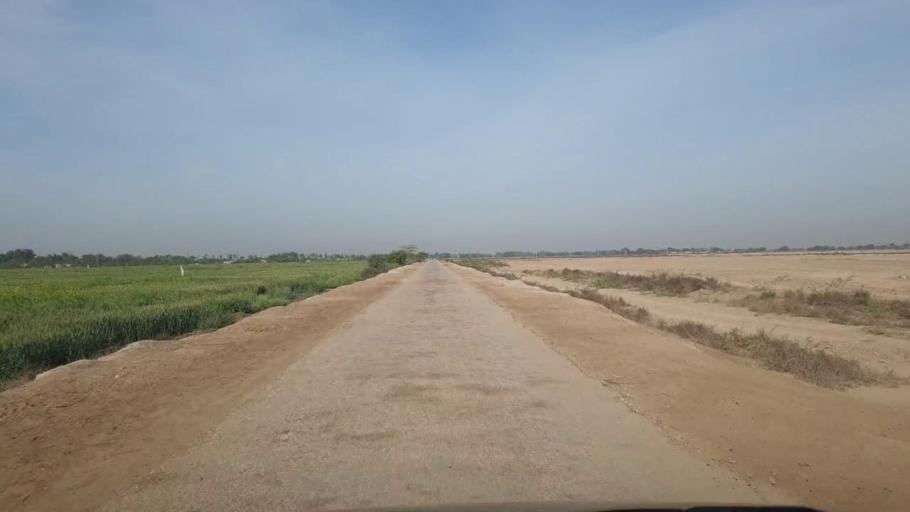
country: PK
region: Sindh
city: Umarkot
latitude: 25.3325
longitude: 69.7094
